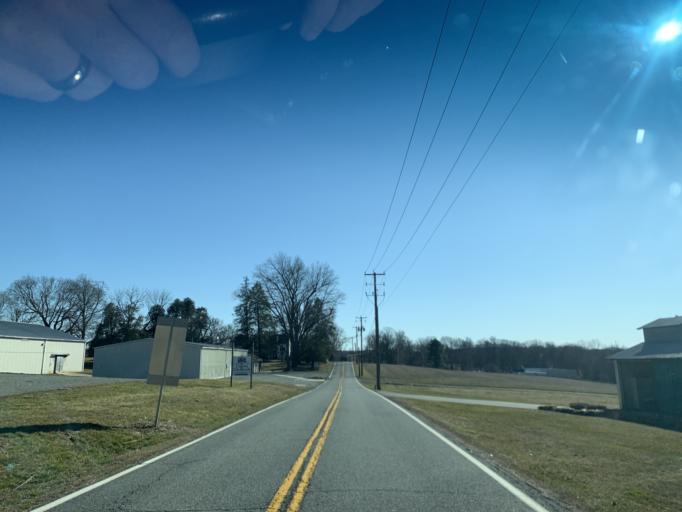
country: US
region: Maryland
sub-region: Cecil County
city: Rising Sun
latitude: 39.6701
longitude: -76.0998
